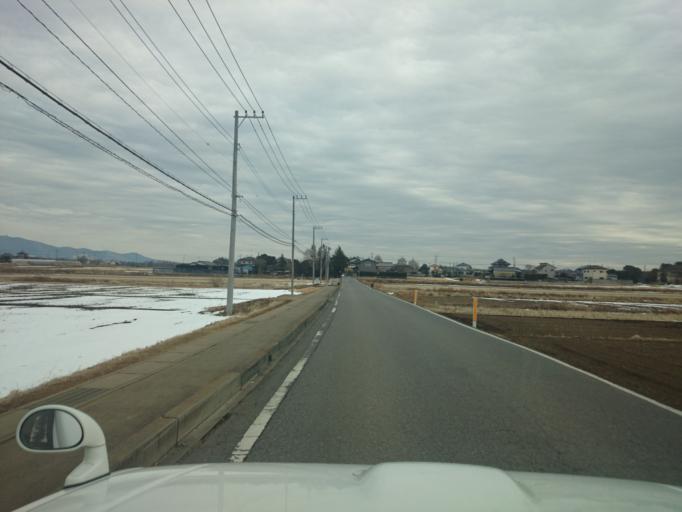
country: JP
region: Ibaraki
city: Ishige
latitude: 36.1107
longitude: 140.0523
